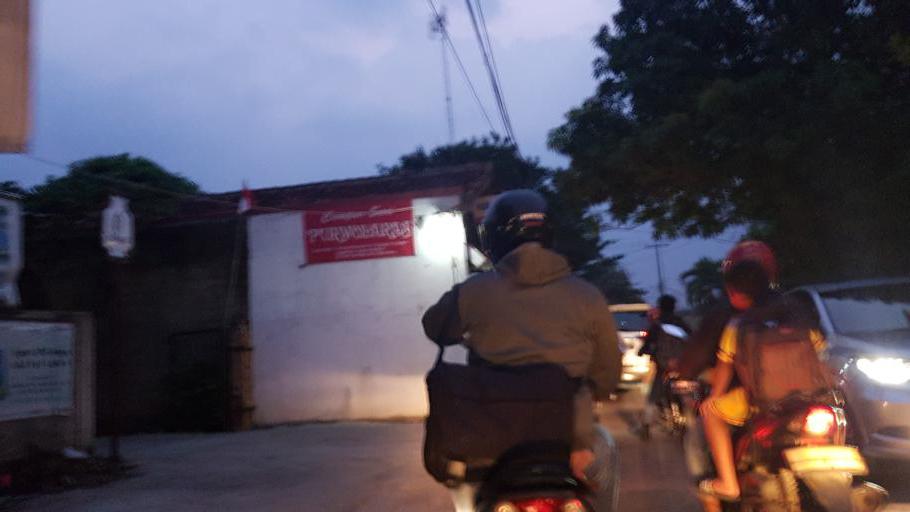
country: ID
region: West Java
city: Depok
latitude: -6.3441
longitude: 106.8009
